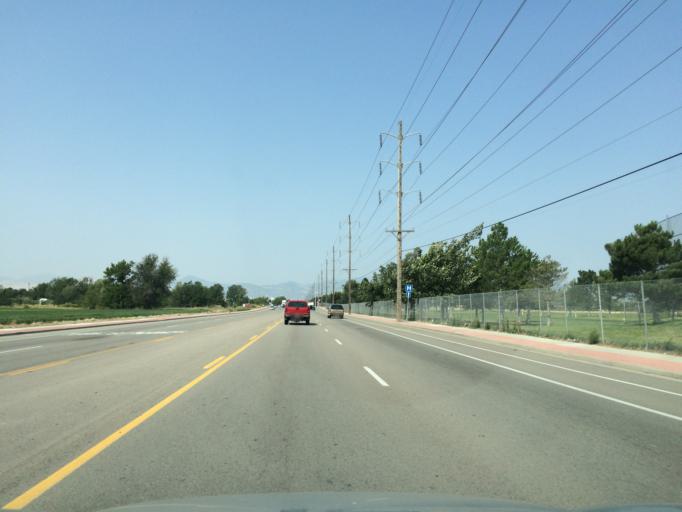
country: US
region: Utah
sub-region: Salt Lake County
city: South Jordan Heights
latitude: 40.5878
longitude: -111.9495
